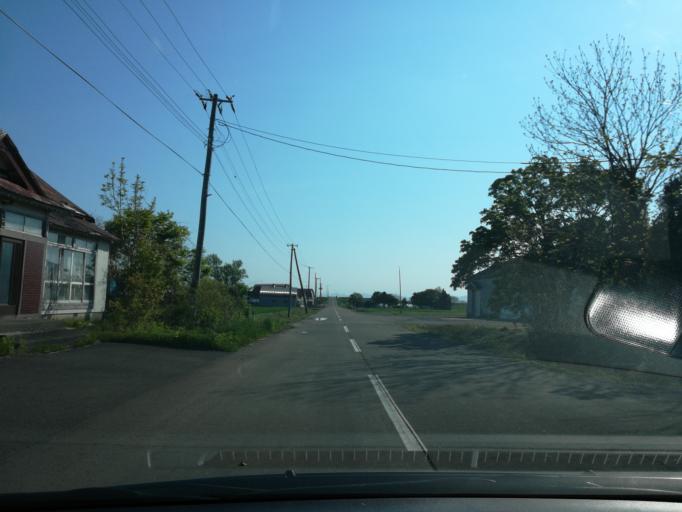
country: JP
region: Hokkaido
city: Iwamizawa
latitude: 43.1296
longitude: 141.6737
